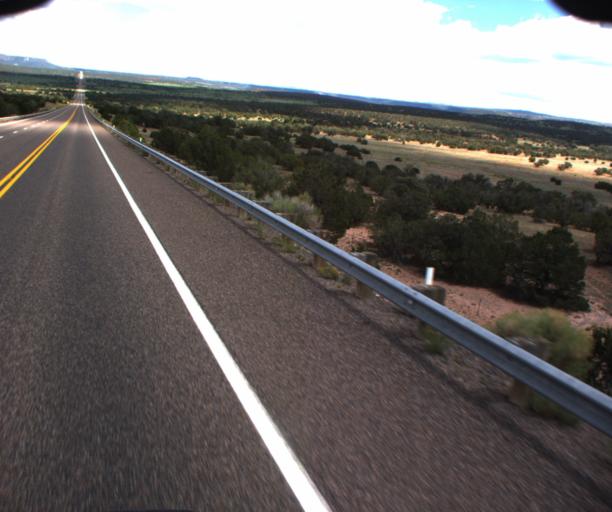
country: US
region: Arizona
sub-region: Apache County
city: Springerville
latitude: 34.1504
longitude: -109.1715
